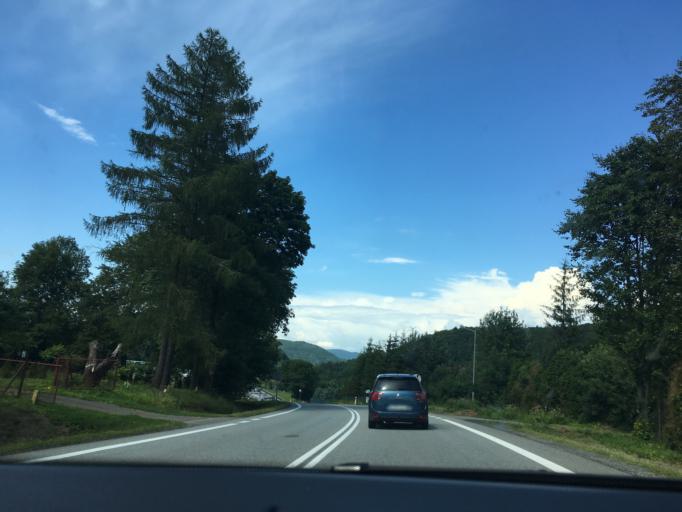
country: PL
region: Subcarpathian Voivodeship
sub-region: Powiat krosnienski
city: Jasliska
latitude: 49.4363
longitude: 21.6905
